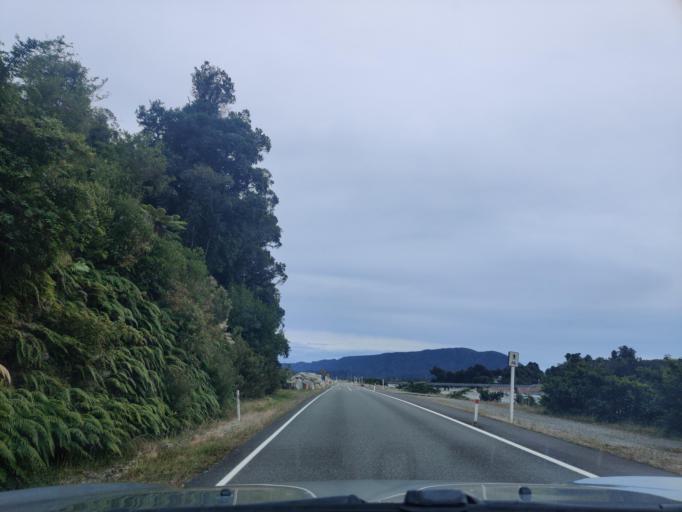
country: NZ
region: West Coast
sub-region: Westland District
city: Hokitika
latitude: -43.3970
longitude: 170.1815
